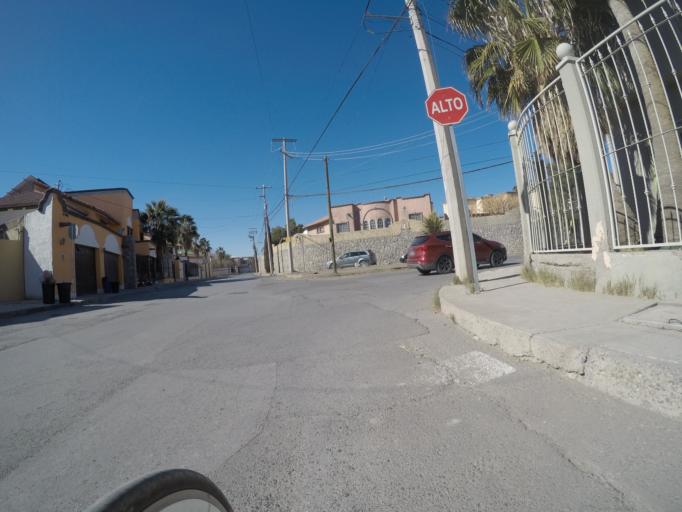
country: MX
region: Chihuahua
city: Ciudad Juarez
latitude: 31.7064
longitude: -106.4138
